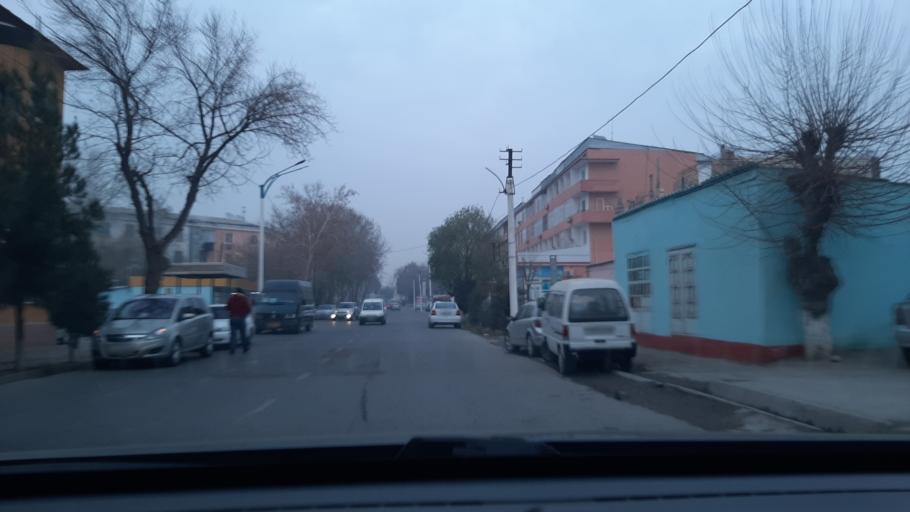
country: TJ
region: Viloyati Sughd
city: Khujand
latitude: 40.2712
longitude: 69.6044
